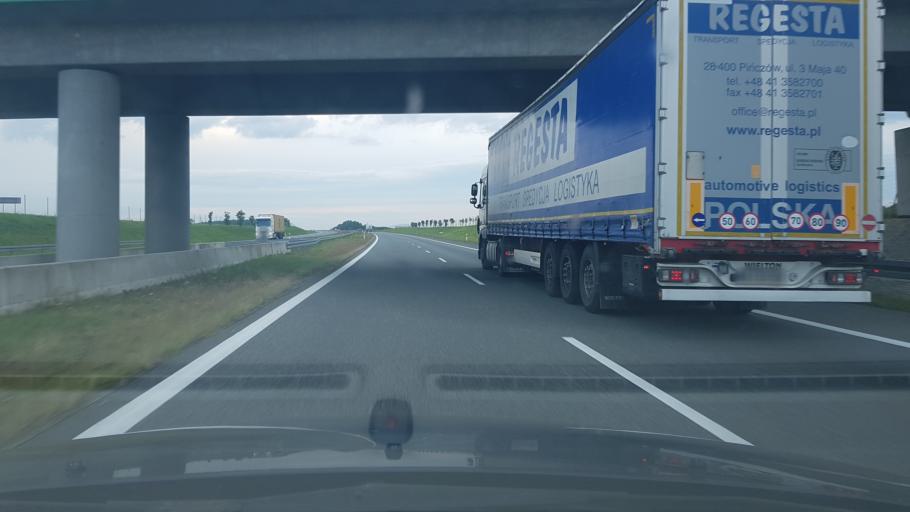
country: PL
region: Warmian-Masurian Voivodeship
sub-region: Powiat ostrodzki
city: Milomlyn
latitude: 53.8273
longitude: 19.7743
